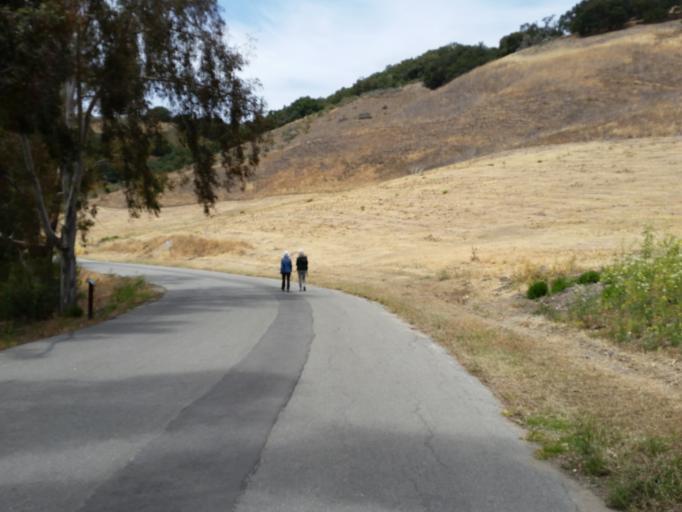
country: US
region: California
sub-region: San Luis Obispo County
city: Avila Beach
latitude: 35.1837
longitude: -120.7303
